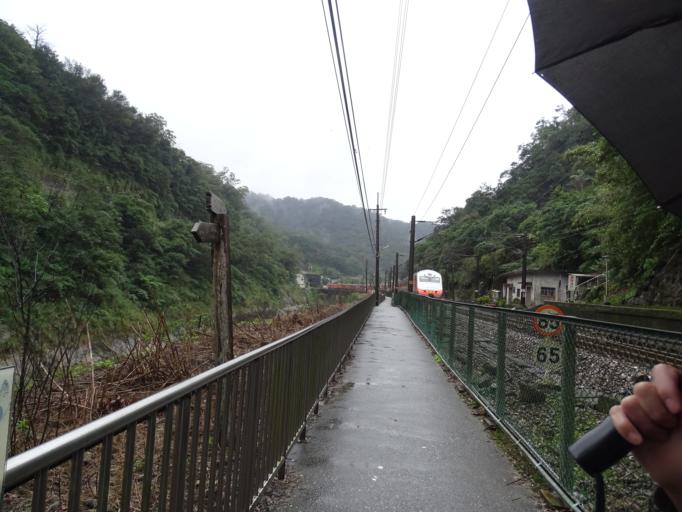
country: TW
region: Taiwan
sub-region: Keelung
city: Keelung
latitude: 25.0647
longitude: 121.8225
